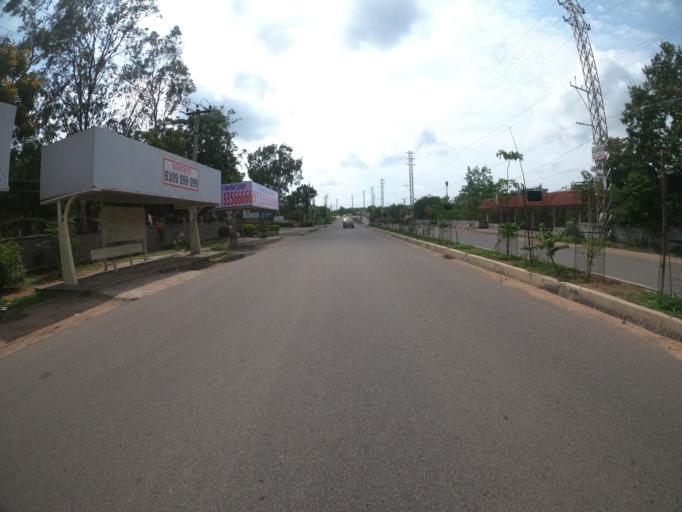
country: IN
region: Telangana
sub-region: Medak
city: Serilingampalle
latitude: 17.3936
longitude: 78.3203
